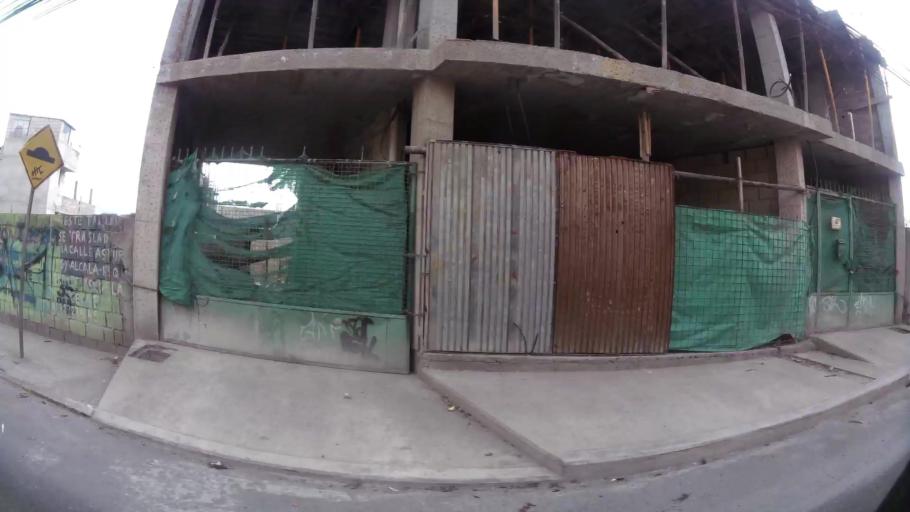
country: EC
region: Pichincha
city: Quito
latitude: -0.0909
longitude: -78.4413
